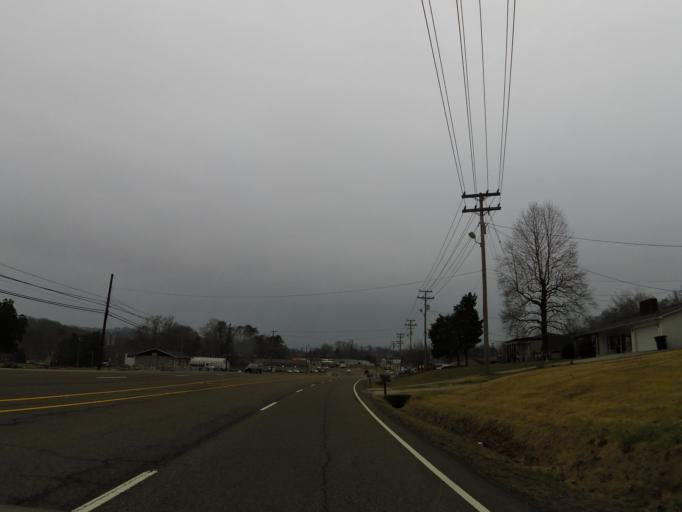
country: US
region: Tennessee
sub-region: Anderson County
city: Clinton
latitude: 36.0850
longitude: -84.1292
